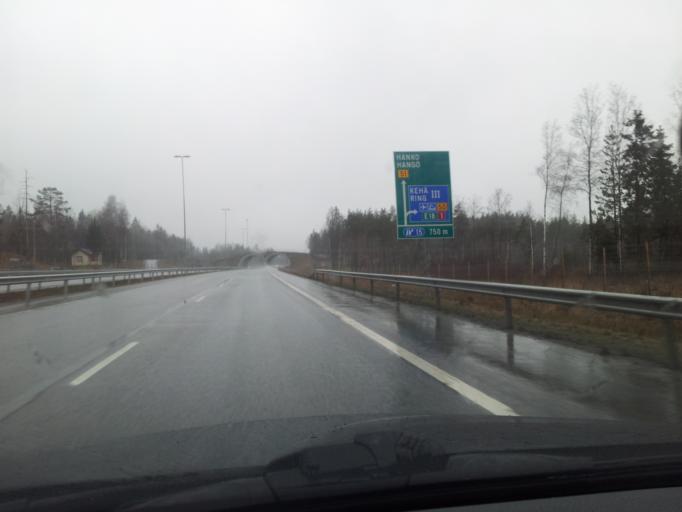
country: FI
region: Uusimaa
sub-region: Helsinki
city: Kirkkonummi
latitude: 60.1413
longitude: 24.5530
